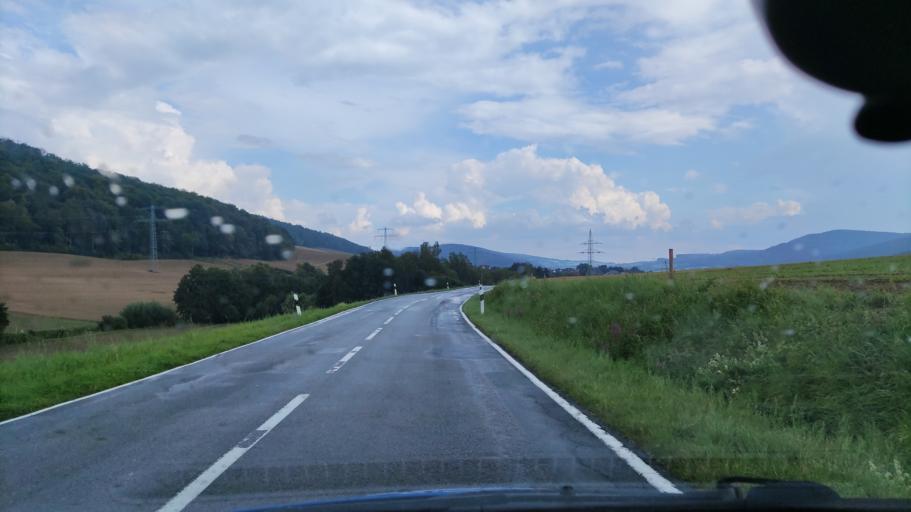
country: DE
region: Lower Saxony
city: Delligsen
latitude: 51.9543
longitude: 9.7892
